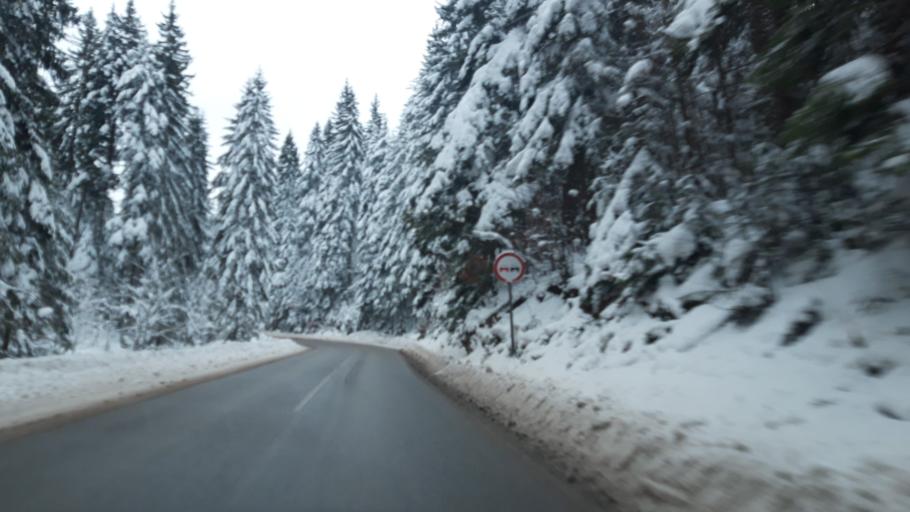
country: BA
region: Republika Srpska
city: Koran
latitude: 43.7547
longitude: 18.5493
